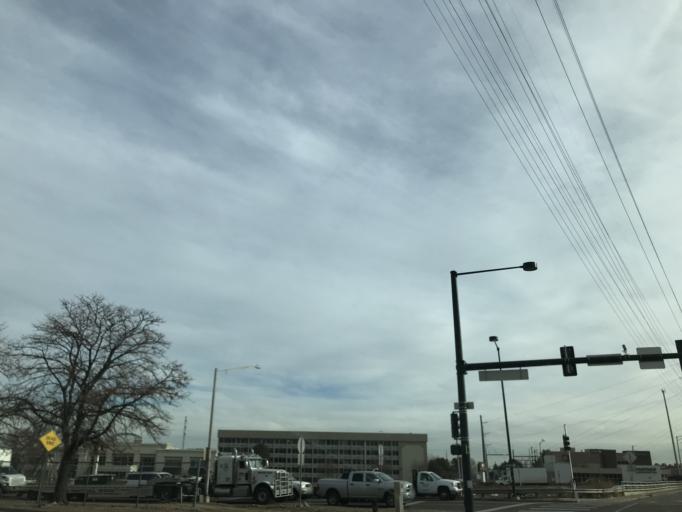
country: US
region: Colorado
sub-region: Adams County
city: Commerce City
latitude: 39.7728
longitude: -104.9040
